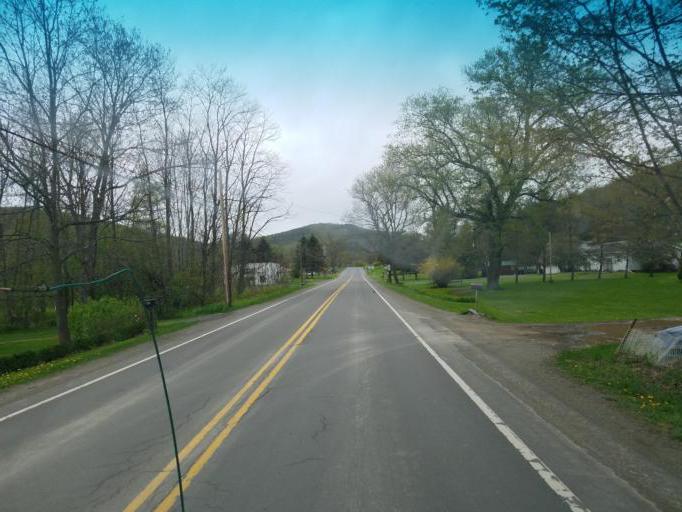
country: US
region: Pennsylvania
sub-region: Tioga County
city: Westfield
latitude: 41.9137
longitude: -77.6056
